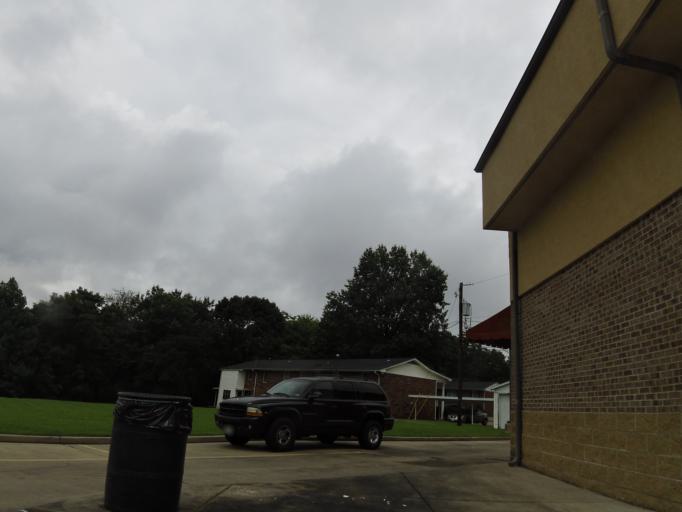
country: US
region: Missouri
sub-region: Cape Girardeau County
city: Cape Girardeau
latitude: 37.3384
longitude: -89.5539
